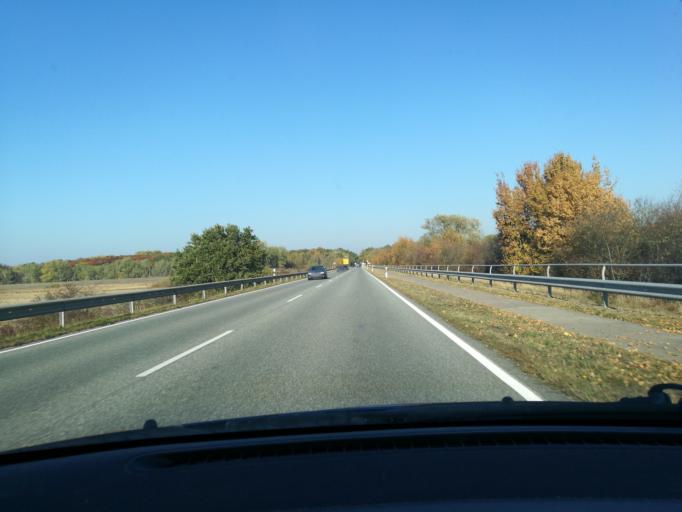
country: DE
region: Mecklenburg-Vorpommern
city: Domitz
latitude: 53.1467
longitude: 11.2310
